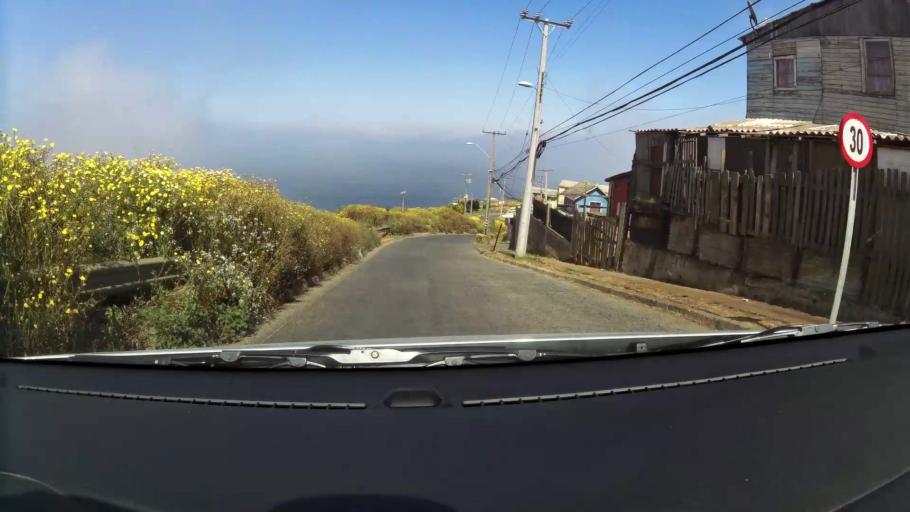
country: CL
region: Valparaiso
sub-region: Provincia de Valparaiso
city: Valparaiso
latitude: -33.0416
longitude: -71.6560
